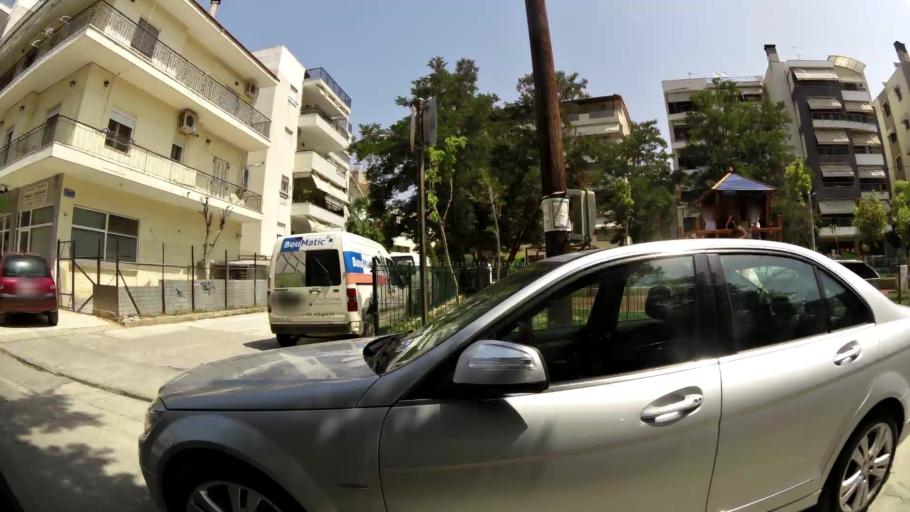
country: GR
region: Central Macedonia
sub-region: Nomos Thessalonikis
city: Evosmos
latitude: 40.6698
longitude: 22.9119
